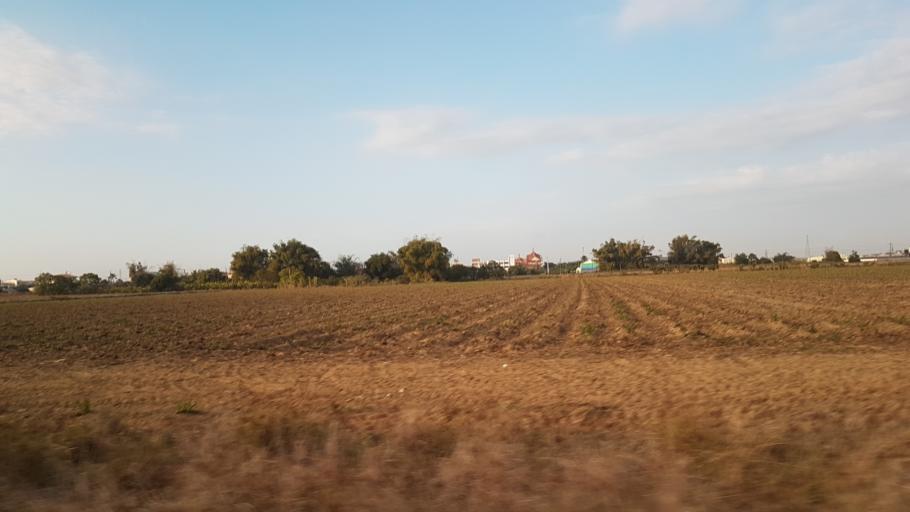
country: TW
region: Taiwan
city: Xinying
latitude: 23.3471
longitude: 120.3686
